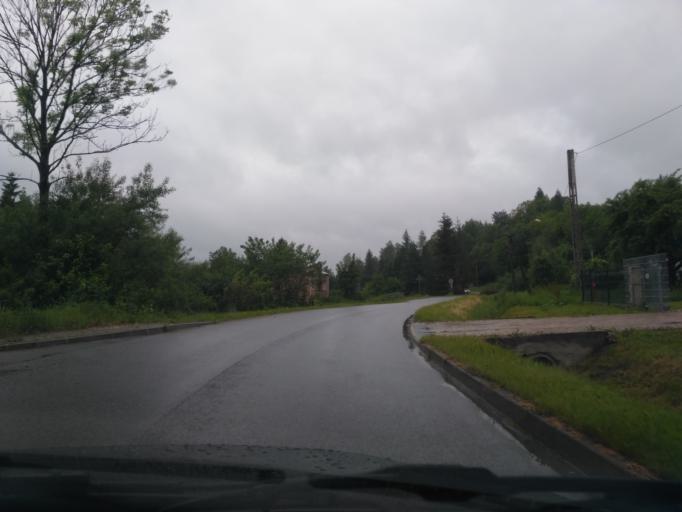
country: PL
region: Lesser Poland Voivodeship
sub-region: Powiat gorlicki
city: Sekowa
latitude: 49.6173
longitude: 21.2055
